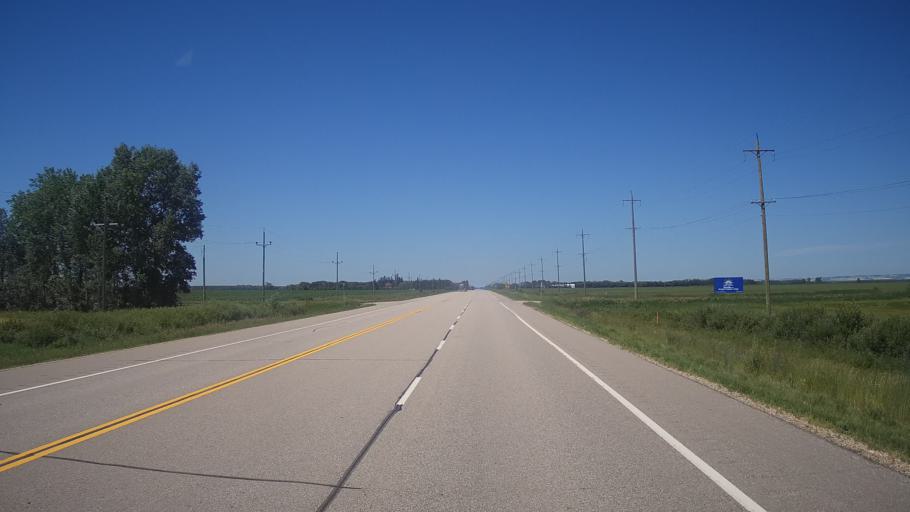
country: CA
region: Manitoba
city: Neepawa
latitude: 50.2252
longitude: -99.2924
